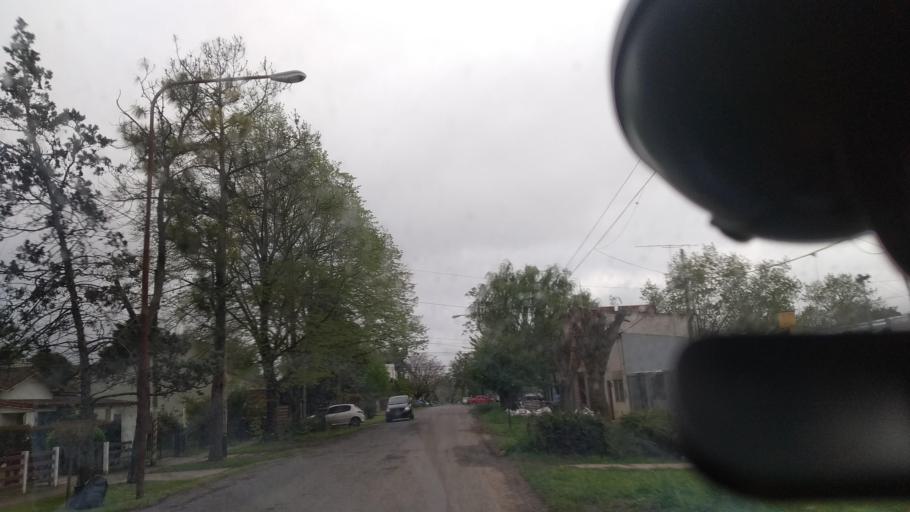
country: AR
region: Buenos Aires
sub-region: Partido de La Plata
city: La Plata
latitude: -34.9545
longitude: -57.9971
